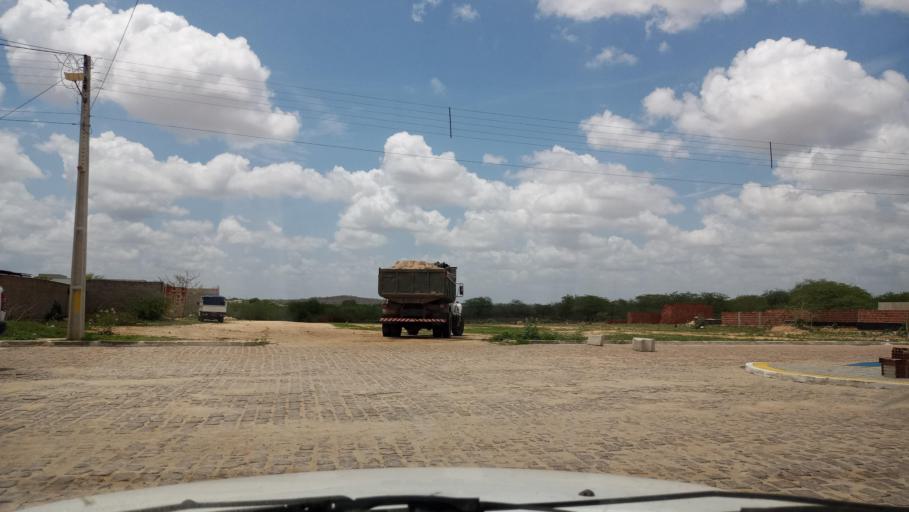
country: BR
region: Rio Grande do Norte
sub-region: Tangara
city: Tangara
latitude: -6.1059
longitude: -35.7148
